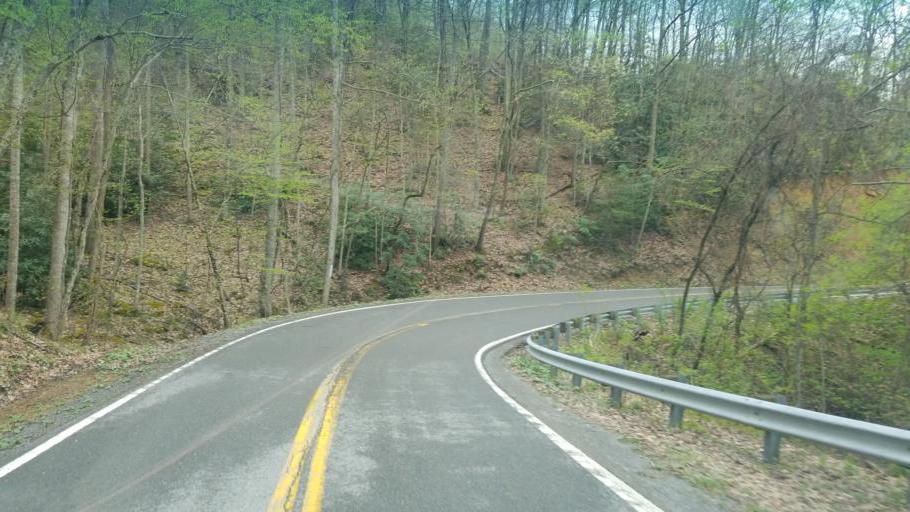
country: US
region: Virginia
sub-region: Tazewell County
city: Tazewell
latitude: 37.0039
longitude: -81.5226
